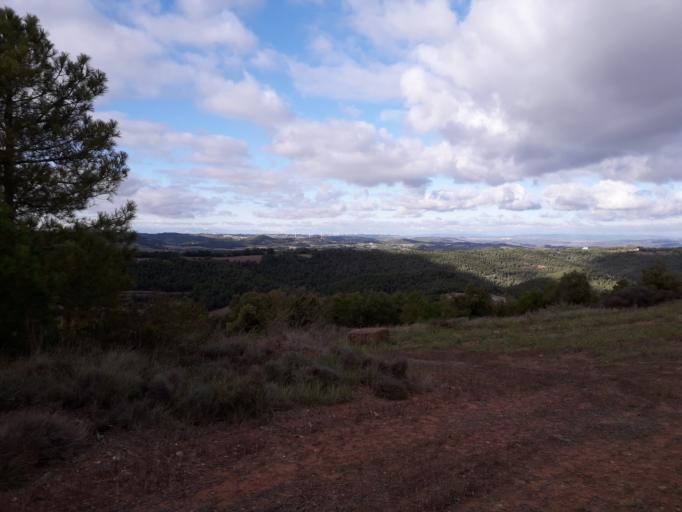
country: ES
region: Catalonia
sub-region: Provincia de Barcelona
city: Bellprat
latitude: 41.5515
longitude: 1.4429
